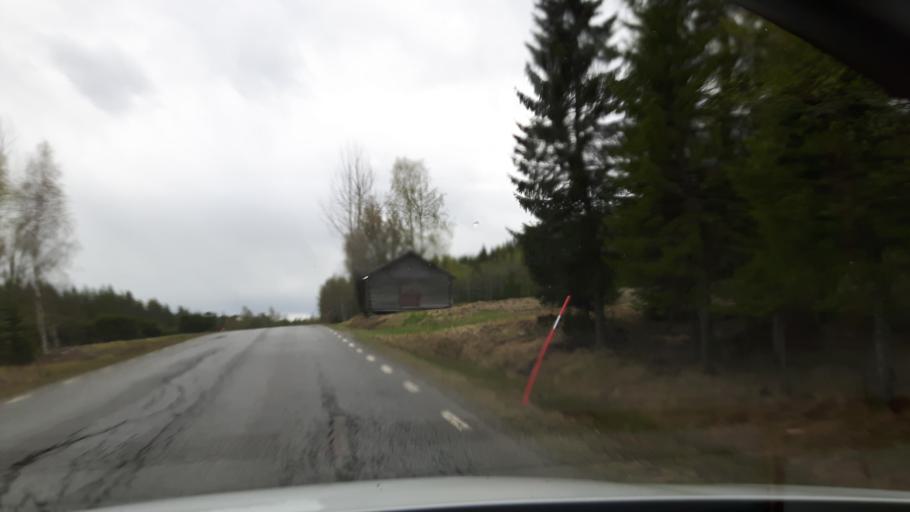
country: SE
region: Vaesterbotten
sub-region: Skelleftea Kommun
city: Burtraesk
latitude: 64.2891
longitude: 20.5249
